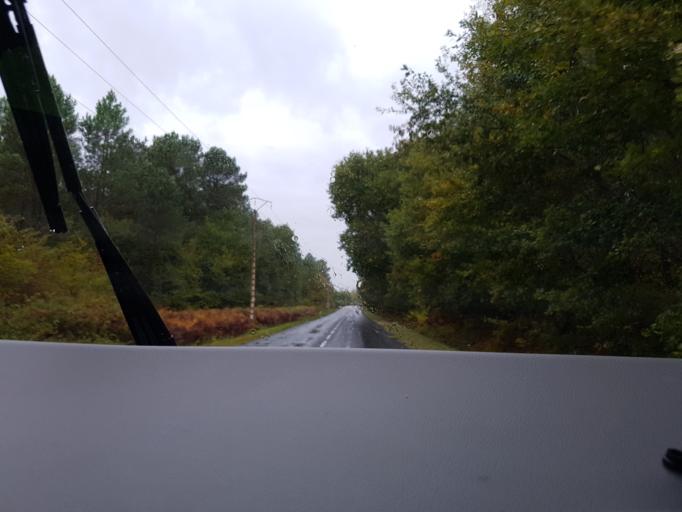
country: FR
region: Aquitaine
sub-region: Departement des Landes
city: Pissos
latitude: 44.3780
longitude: -0.6755
